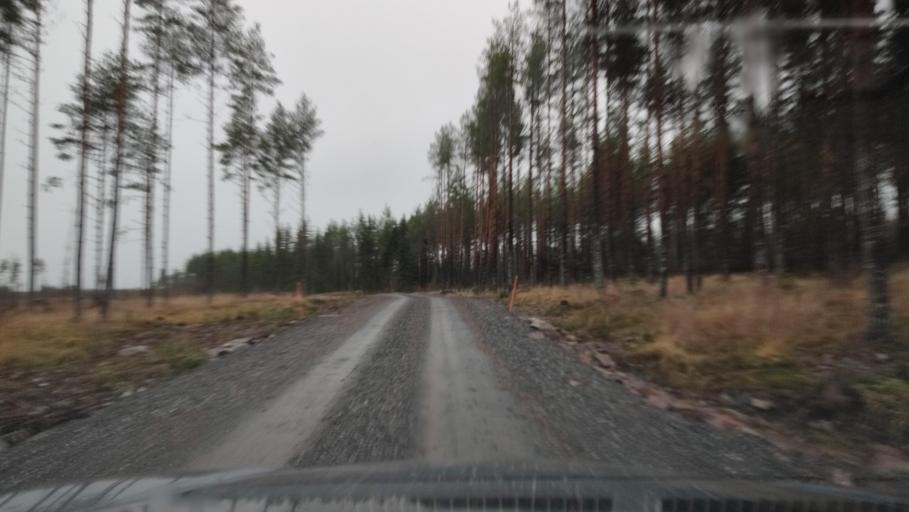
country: FI
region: Southern Ostrobothnia
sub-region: Suupohja
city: Karijoki
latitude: 62.1787
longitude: 21.6021
